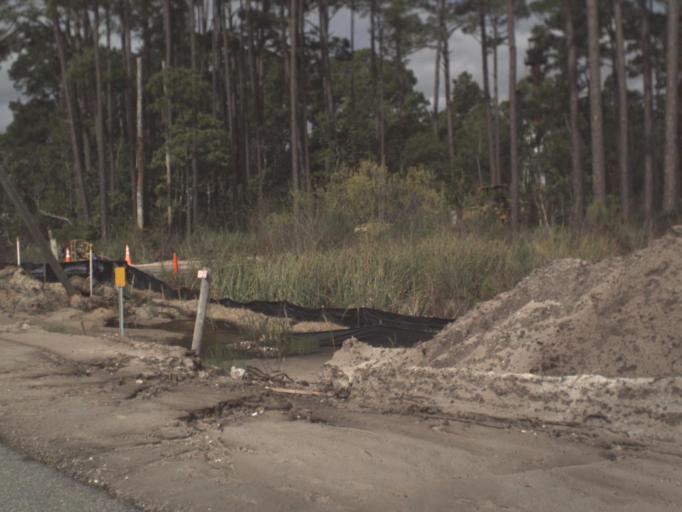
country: US
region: Florida
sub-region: Franklin County
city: Carrabelle
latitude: 29.8262
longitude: -84.6991
